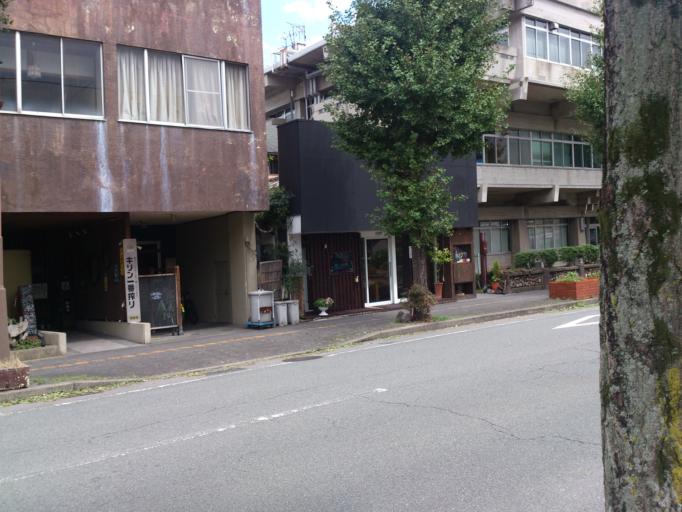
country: JP
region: Yamaguchi
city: Yamaguchi-shi
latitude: 34.1741
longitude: 131.4791
